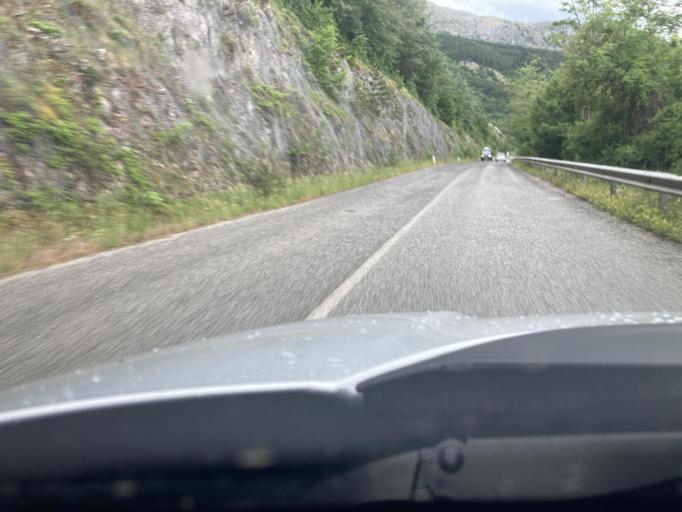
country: IT
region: Abruzzo
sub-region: Provincia dell' Aquila
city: San Panfilo d'Ocre
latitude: 42.2777
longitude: 13.4692
